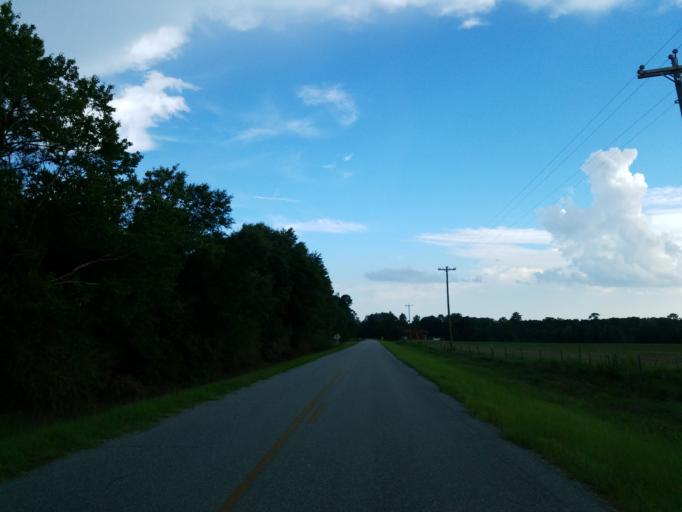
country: US
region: Georgia
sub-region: Tift County
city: Omega
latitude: 31.2626
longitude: -83.5141
